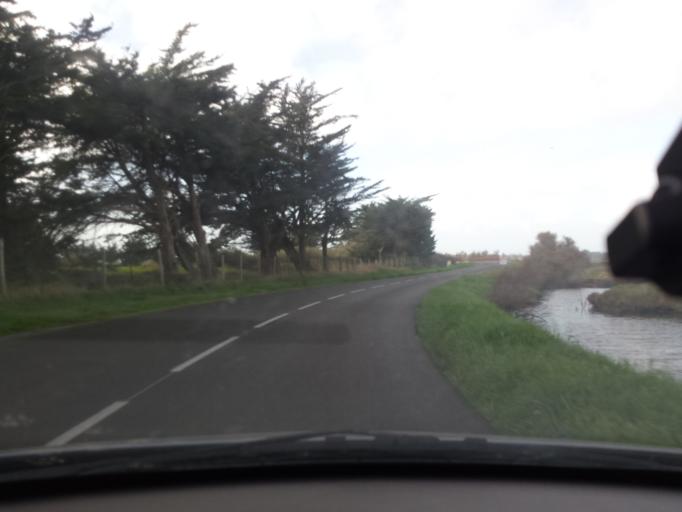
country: FR
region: Pays de la Loire
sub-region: Departement de la Vendee
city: Olonne-sur-Mer
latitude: 46.5553
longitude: -1.7896
